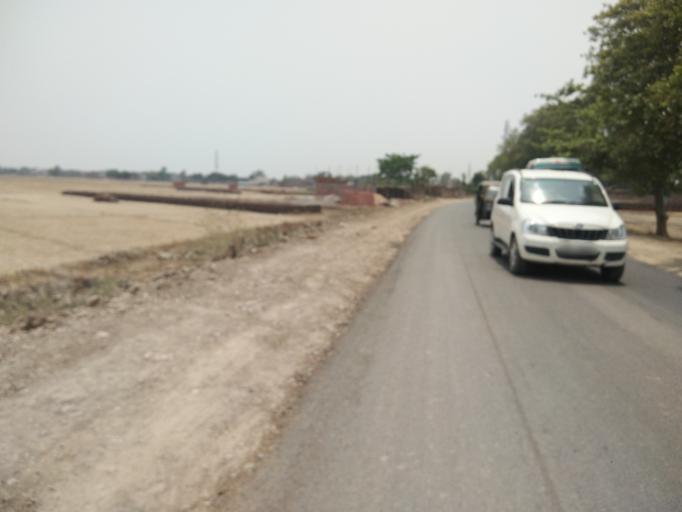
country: IN
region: Uttar Pradesh
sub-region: Ghazipur
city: Zamania
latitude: 25.4342
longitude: 83.6772
